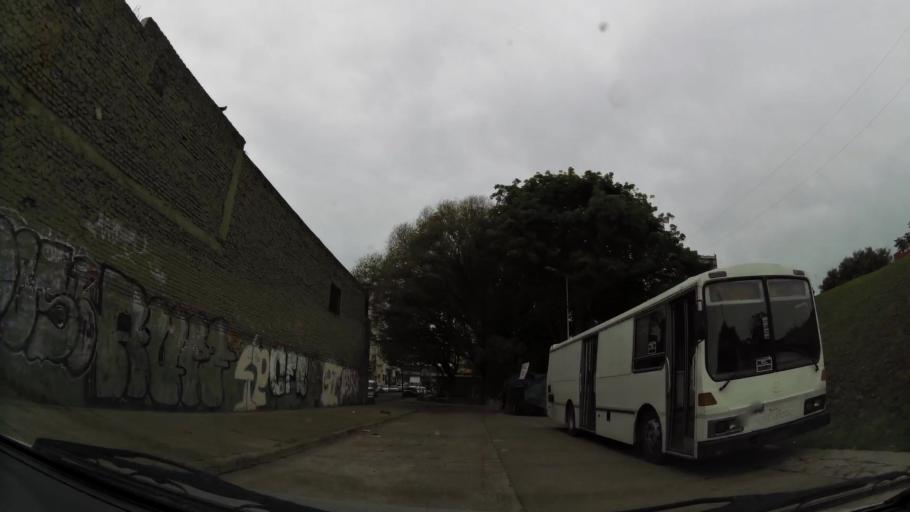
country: AR
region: Buenos Aires
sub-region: Partido de Avellaneda
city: Avellaneda
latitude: -34.6649
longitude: -58.3576
